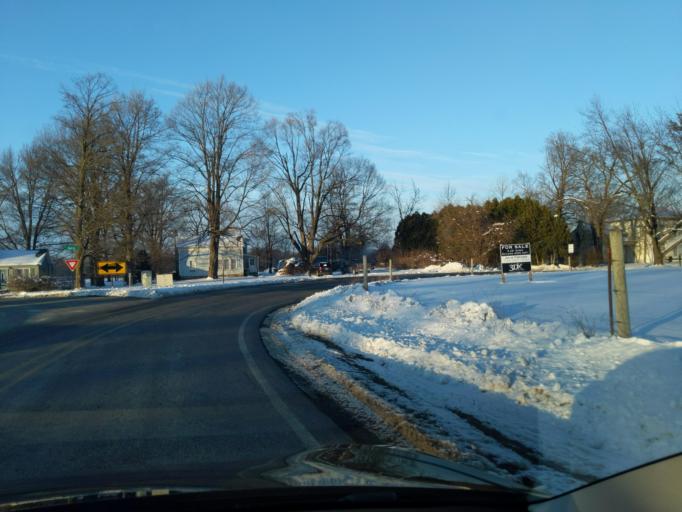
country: US
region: Michigan
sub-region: Livingston County
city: Fowlerville
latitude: 42.5675
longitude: -84.1131
